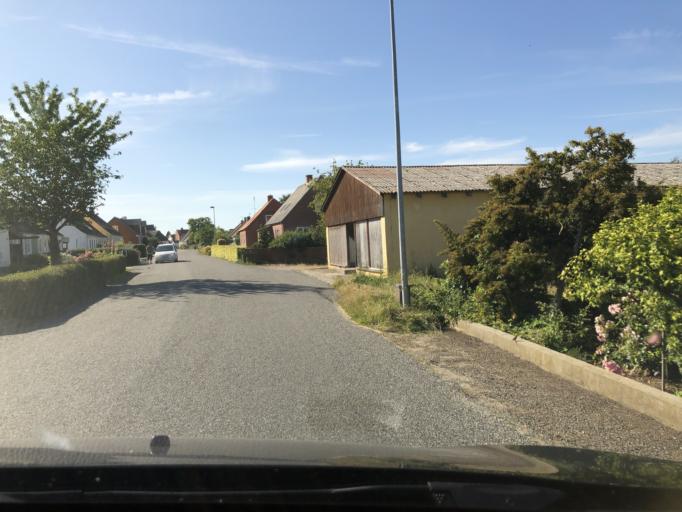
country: DK
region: South Denmark
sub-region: AEro Kommune
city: Marstal
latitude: 54.8711
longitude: 10.4922
